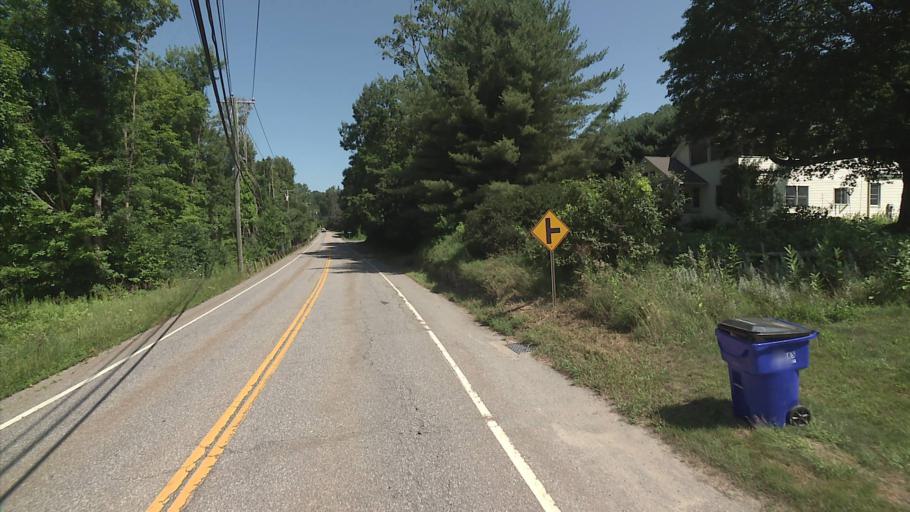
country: US
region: Connecticut
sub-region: Litchfield County
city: New Preston
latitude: 41.6998
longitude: -73.3443
